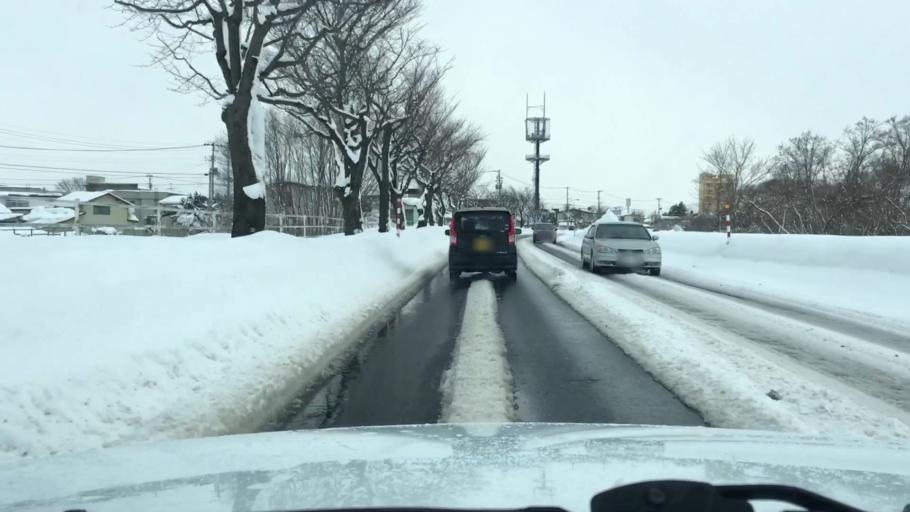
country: JP
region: Aomori
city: Hirosaki
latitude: 40.6118
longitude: 140.4547
